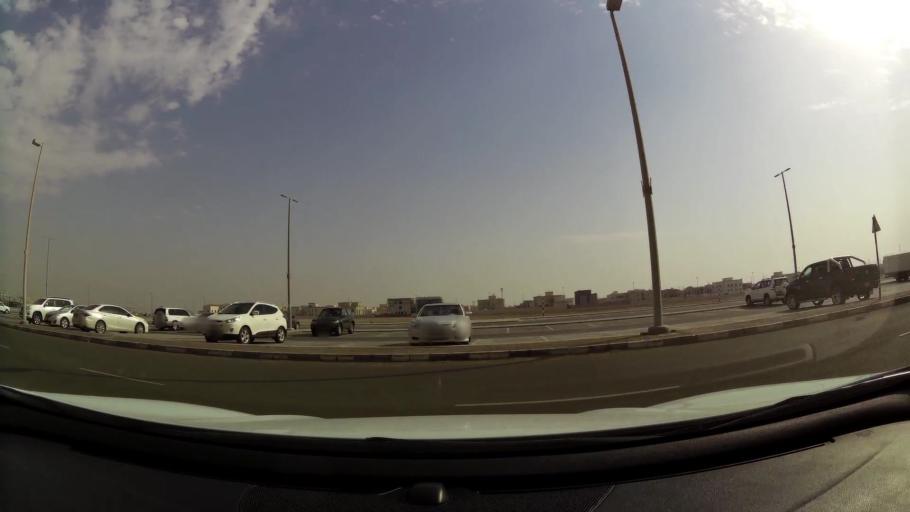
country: AE
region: Abu Dhabi
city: Abu Dhabi
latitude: 24.3178
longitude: 54.5361
